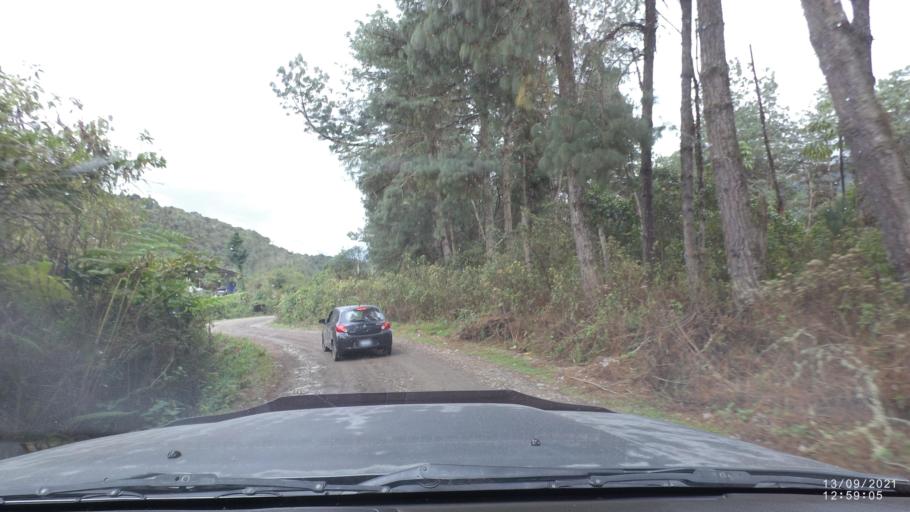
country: BO
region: Cochabamba
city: Colomi
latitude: -17.2359
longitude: -65.8173
